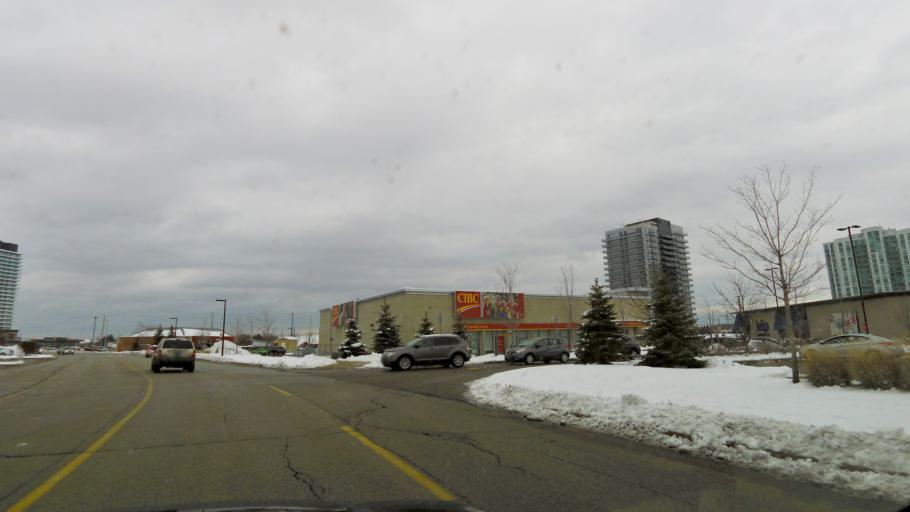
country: CA
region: Ontario
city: Mississauga
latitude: 43.5558
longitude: -79.7130
